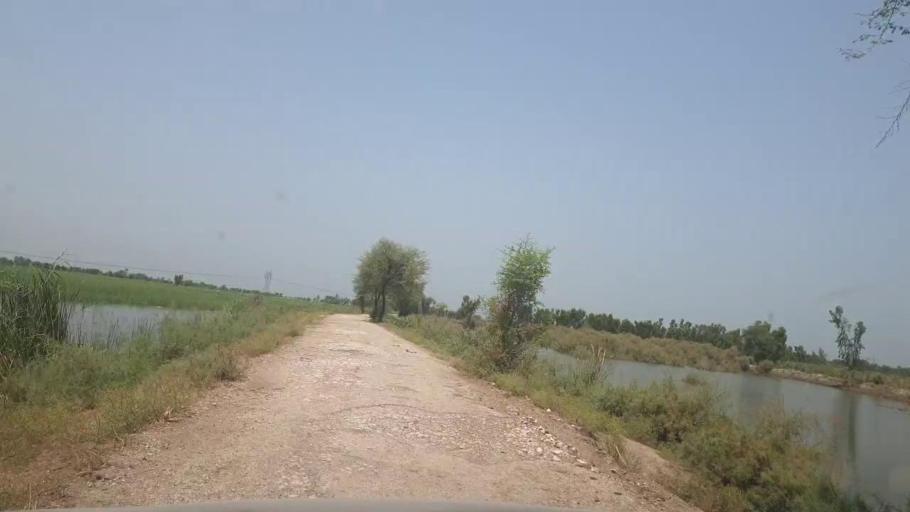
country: PK
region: Sindh
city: Lakhi
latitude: 27.8565
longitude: 68.6246
